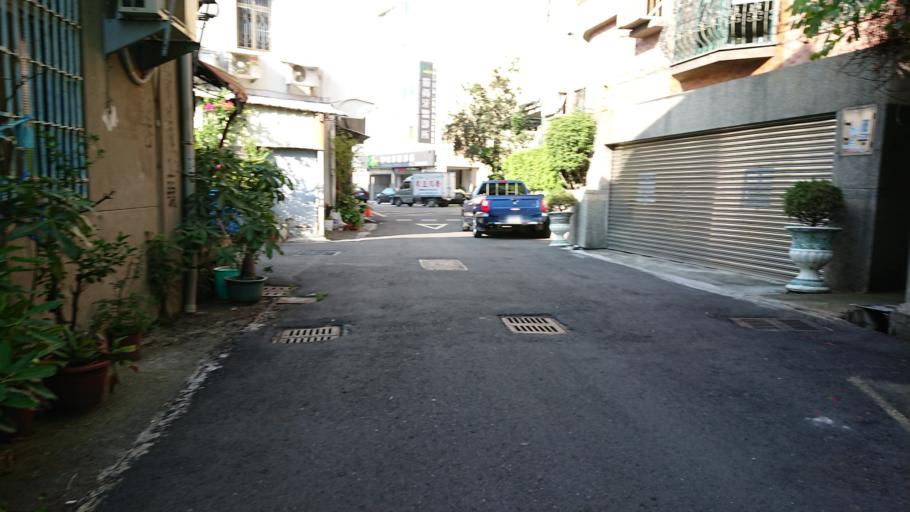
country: TW
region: Taiwan
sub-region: Changhua
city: Chang-hua
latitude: 24.0830
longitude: 120.5538
